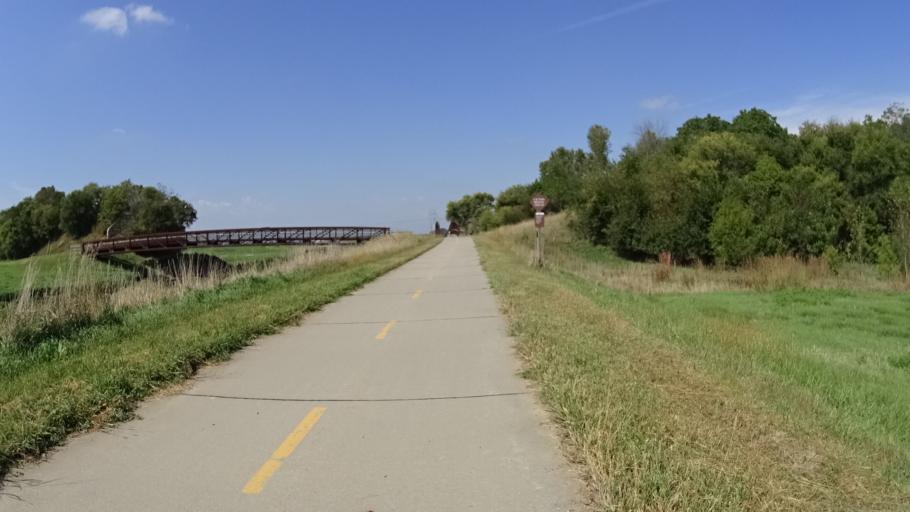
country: US
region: Nebraska
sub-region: Sarpy County
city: Offutt Air Force Base
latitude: 41.1503
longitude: -95.9683
